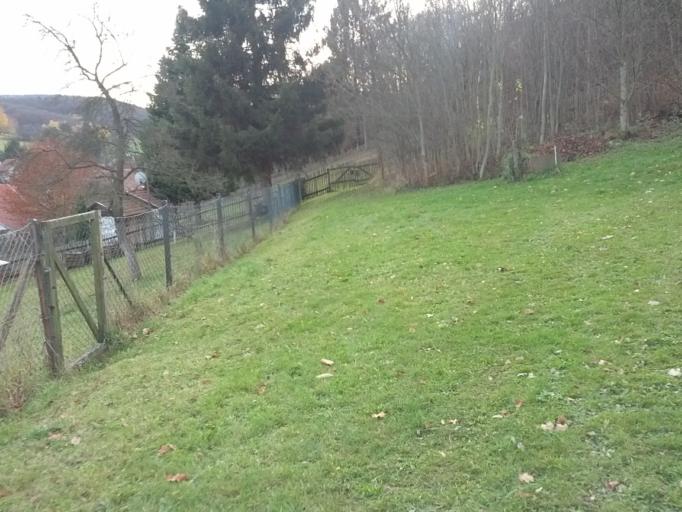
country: DE
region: Thuringia
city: Thal
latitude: 50.9338
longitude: 10.3551
